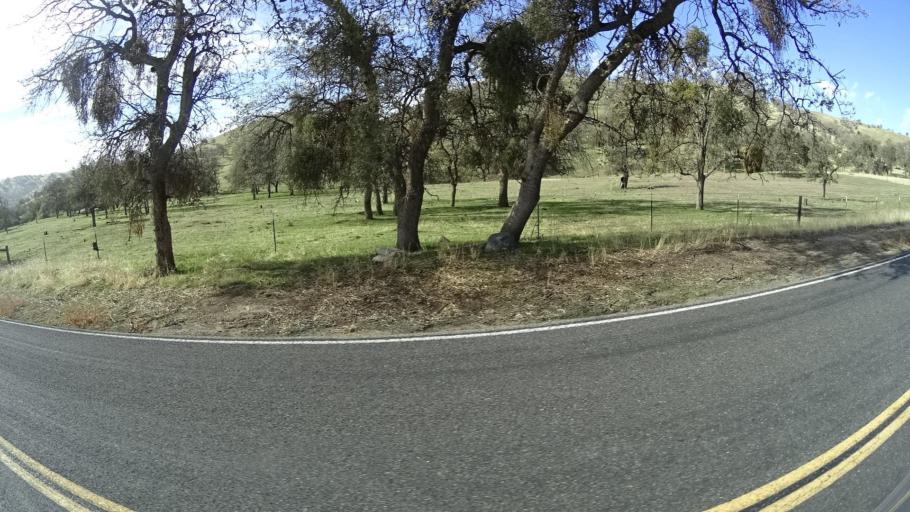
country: US
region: California
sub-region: Kern County
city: Alta Sierra
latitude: 35.6333
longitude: -118.8006
